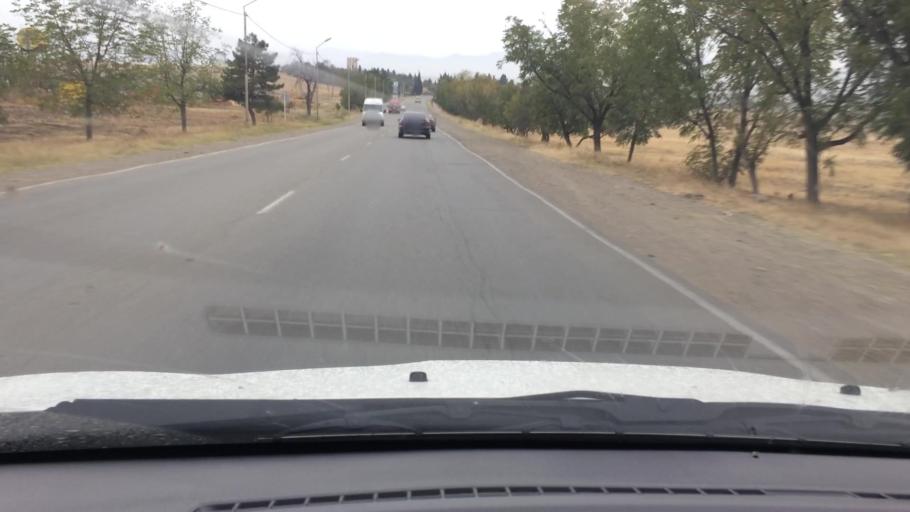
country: GE
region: Kvemo Kartli
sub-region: Marneuli
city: Marneuli
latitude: 41.5181
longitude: 44.7826
